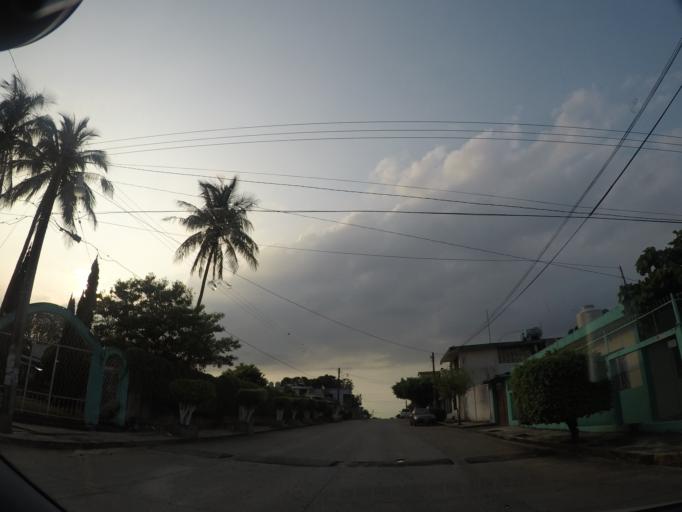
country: MX
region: Oaxaca
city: Matias Romero
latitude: 16.8724
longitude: -95.0418
